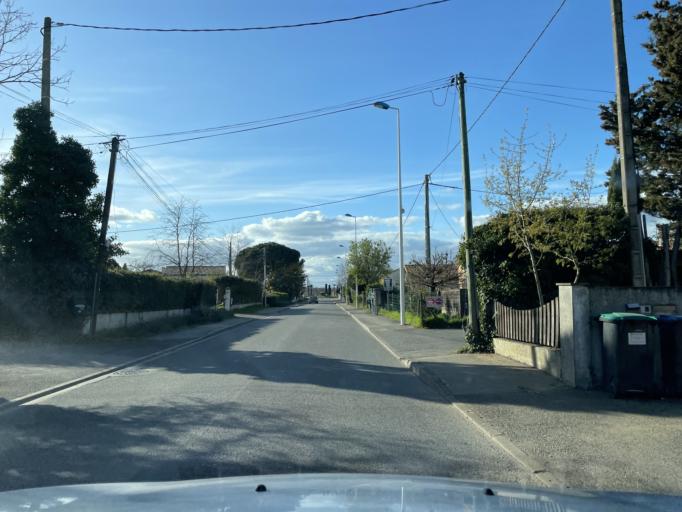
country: FR
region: Midi-Pyrenees
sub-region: Departement de la Haute-Garonne
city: Leguevin
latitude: 43.6020
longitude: 1.2286
